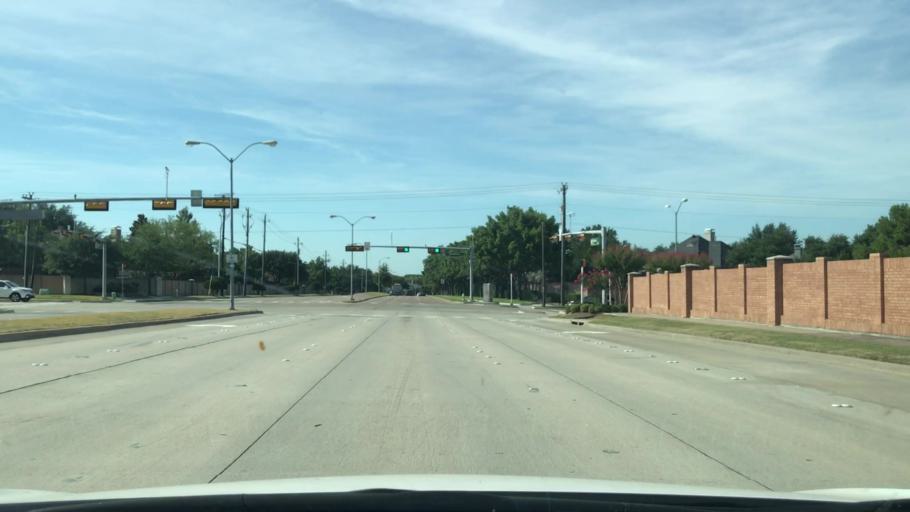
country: US
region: Texas
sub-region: Denton County
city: The Colony
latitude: 33.0574
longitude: -96.8385
